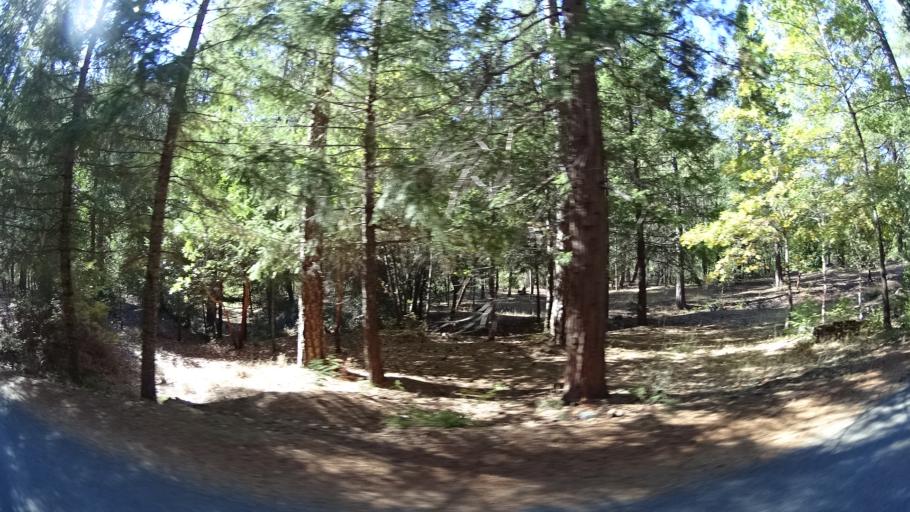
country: US
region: California
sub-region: Trinity County
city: Weaverville
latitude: 41.1428
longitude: -123.1541
